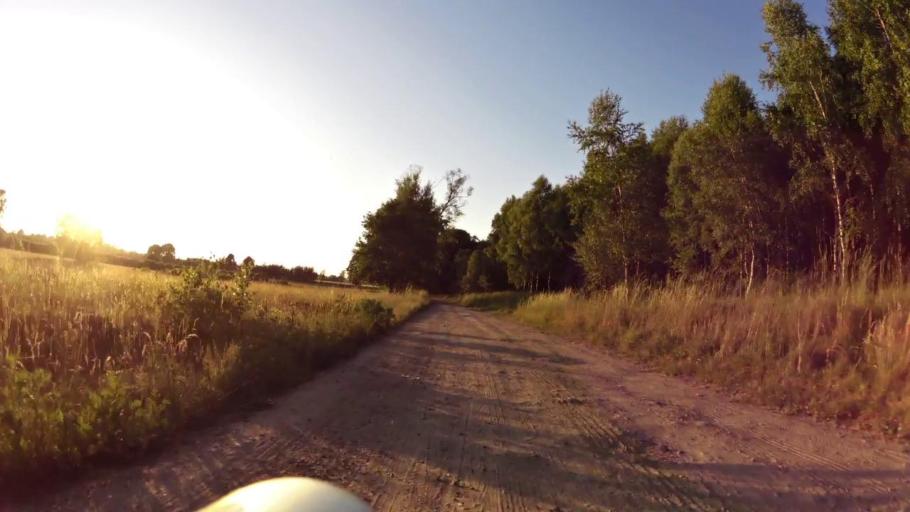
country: PL
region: West Pomeranian Voivodeship
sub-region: Powiat szczecinecki
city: Szczecinek
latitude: 53.8419
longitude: 16.6906
